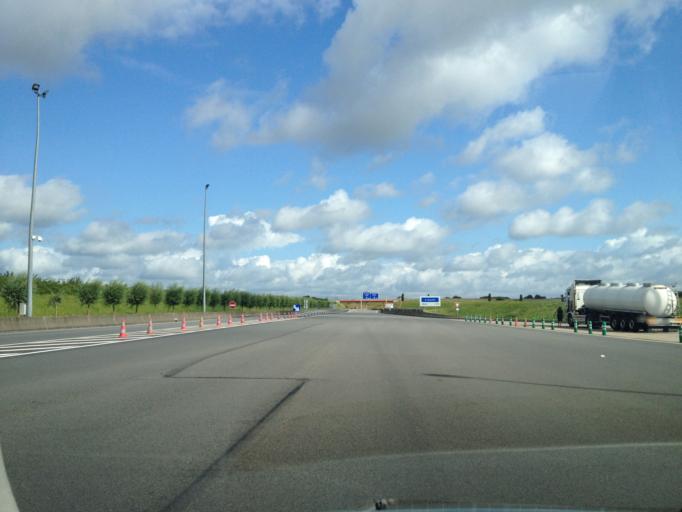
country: FR
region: Haute-Normandie
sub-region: Departement de l'Eure
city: Bourg-Achard
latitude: 49.3545
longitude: 0.8352
